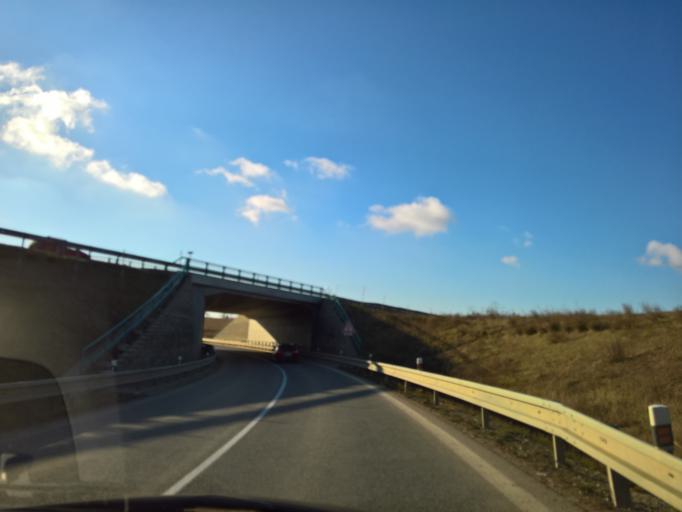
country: SK
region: Nitriansky
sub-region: Okres Nitra
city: Nitra
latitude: 48.2957
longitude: 18.0312
